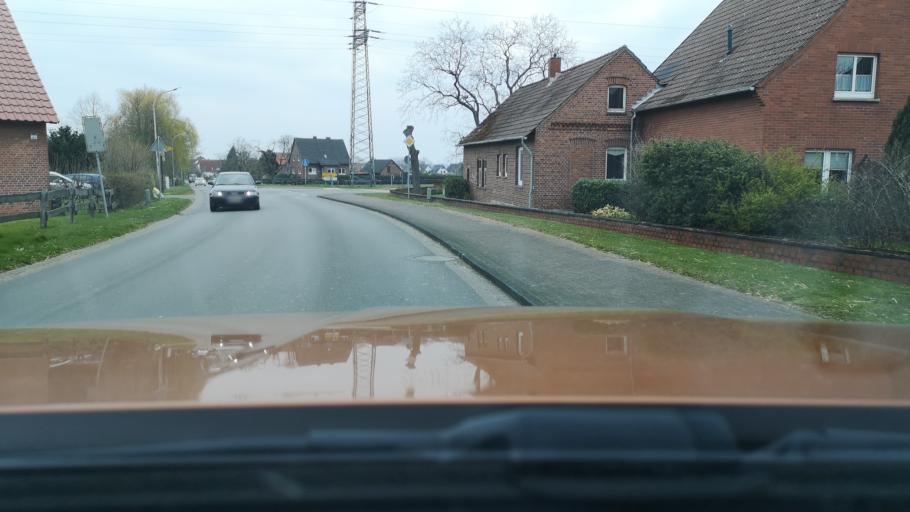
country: DE
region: Lower Saxony
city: Obernkirchen
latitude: 52.2831
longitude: 9.1213
